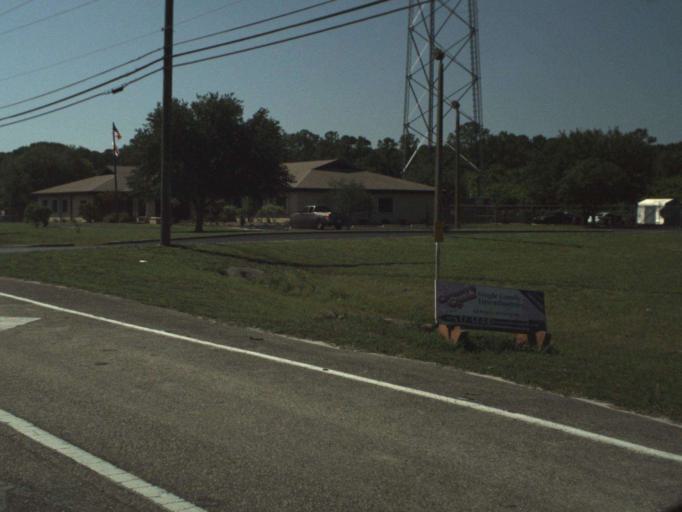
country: US
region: Florida
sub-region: Brevard County
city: Cocoa West
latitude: 28.3580
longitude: -80.7830
